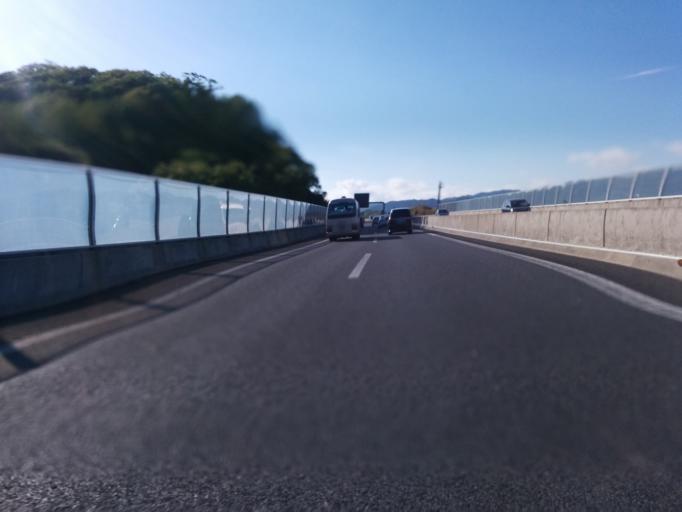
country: JP
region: Shiga Prefecture
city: Kusatsu
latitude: 34.9658
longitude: 135.9629
